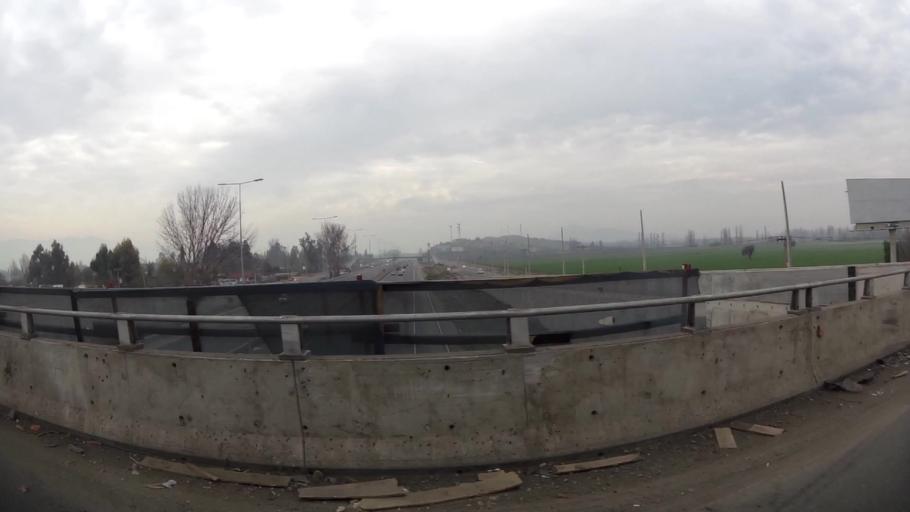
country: CL
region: Santiago Metropolitan
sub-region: Provincia de Chacabuco
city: Chicureo Abajo
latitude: -33.2586
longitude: -70.7484
